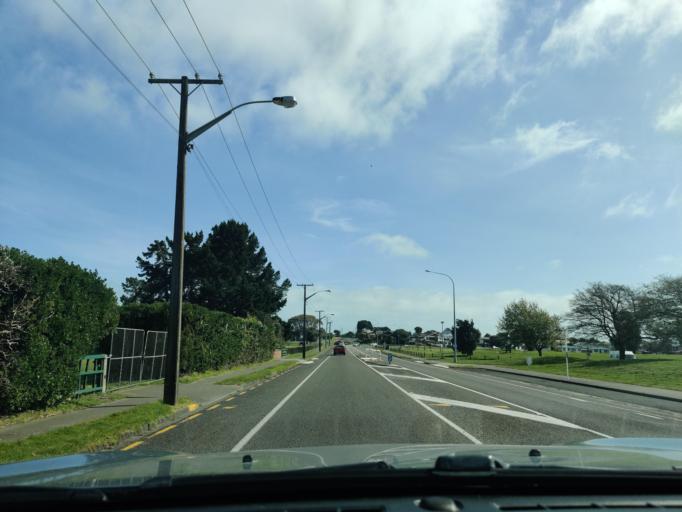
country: NZ
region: Manawatu-Wanganui
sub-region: Wanganui District
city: Wanganui
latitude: -39.9310
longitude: 175.0307
